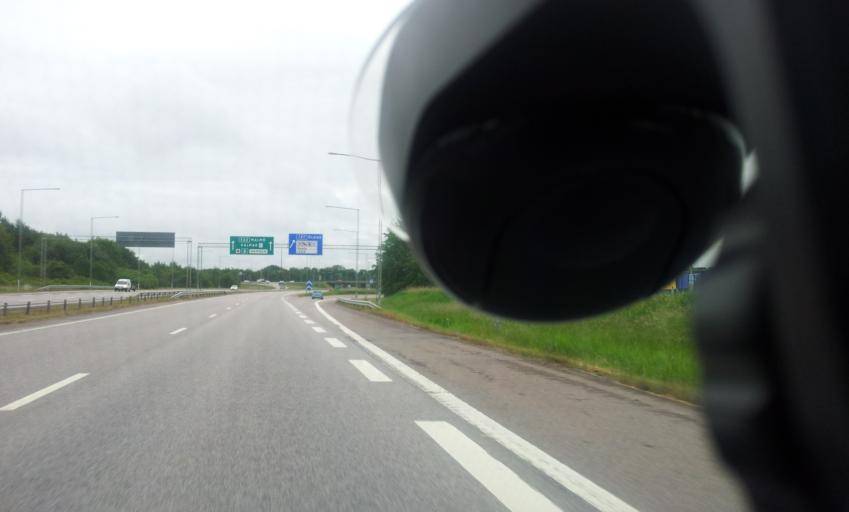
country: SE
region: Kalmar
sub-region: Kalmar Kommun
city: Kalmar
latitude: 56.6876
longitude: 16.3224
